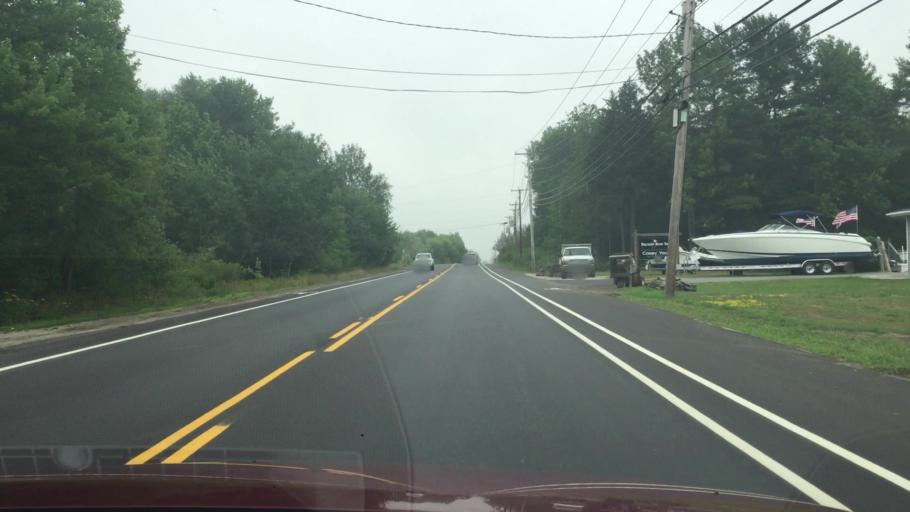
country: US
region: Maine
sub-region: Cumberland County
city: Freeport
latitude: 43.8310
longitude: -70.1314
